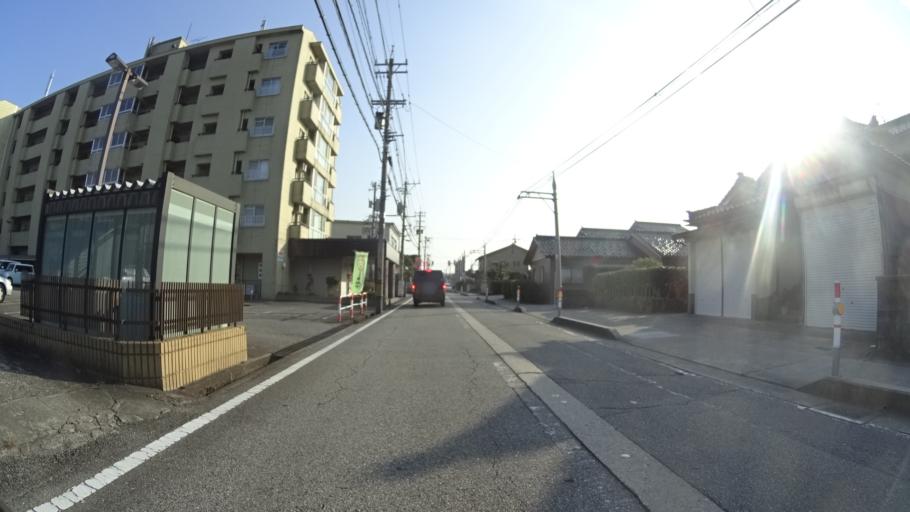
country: JP
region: Toyama
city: Toyama-shi
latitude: 36.7012
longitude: 137.2645
